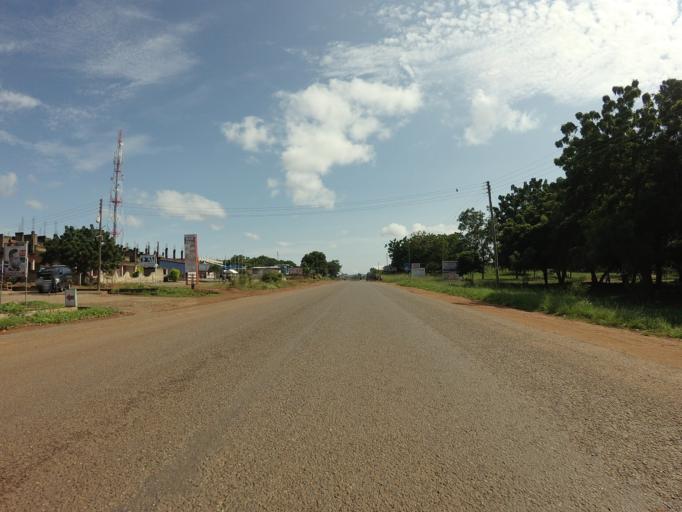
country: GH
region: Eastern
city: Aburi
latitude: 5.8055
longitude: -0.1250
